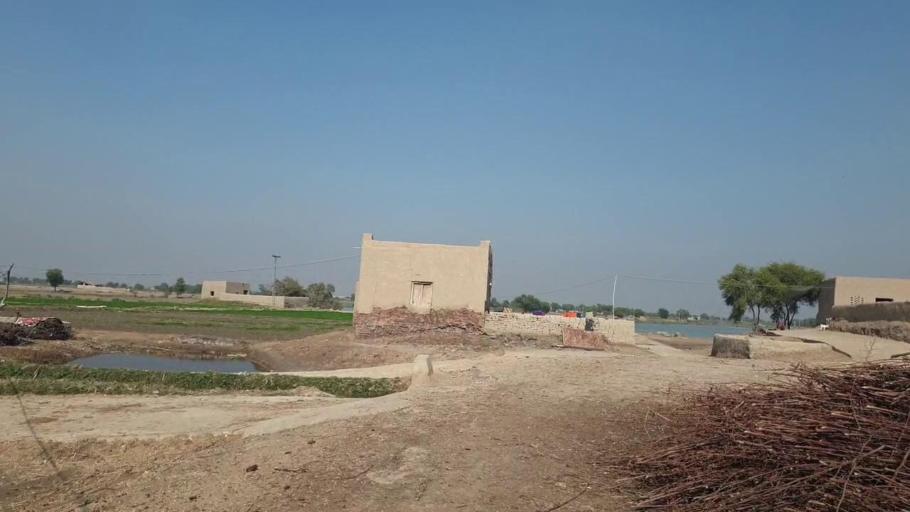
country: PK
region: Sindh
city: Sehwan
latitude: 26.4251
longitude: 67.8103
